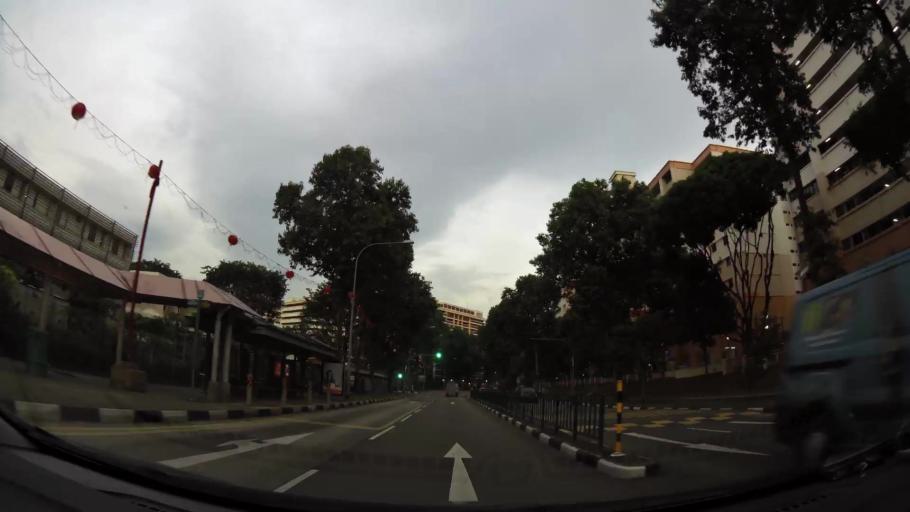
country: MY
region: Johor
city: Kampung Pasir Gudang Baru
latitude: 1.4348
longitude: 103.8302
